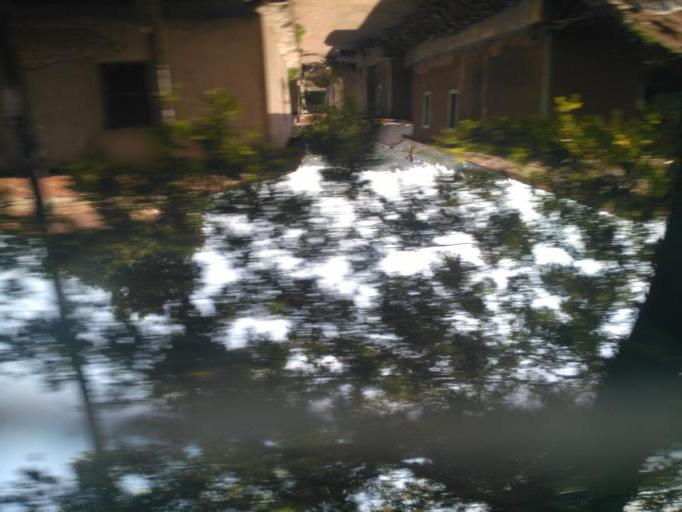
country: TZ
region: Mwanza
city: Mwanza
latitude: -2.5012
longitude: 32.8963
